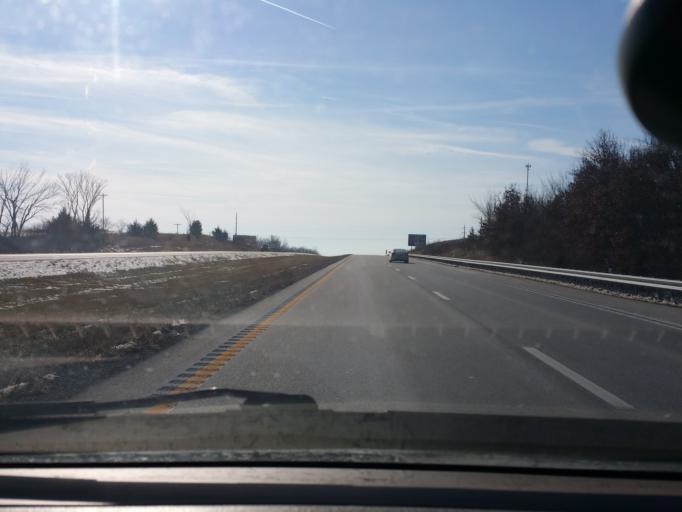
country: US
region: Missouri
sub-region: Clinton County
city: Cameron
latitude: 39.7672
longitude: -94.2153
